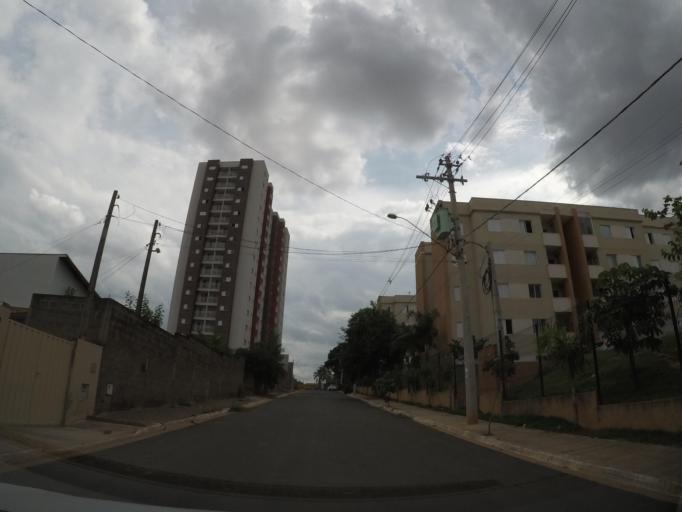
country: BR
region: Sao Paulo
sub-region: Sumare
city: Sumare
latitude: -22.8086
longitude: -47.2425
